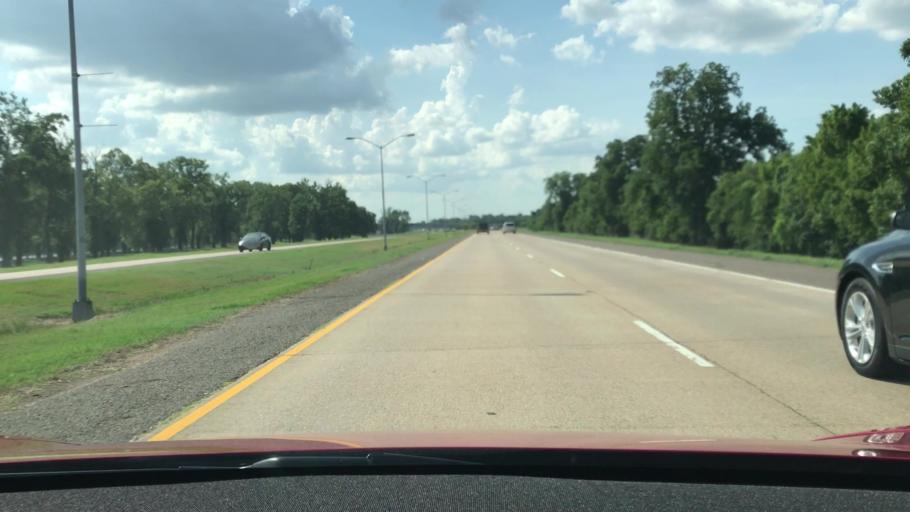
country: US
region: Louisiana
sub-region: Bossier Parish
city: Bossier City
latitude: 32.4862
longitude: -93.6878
